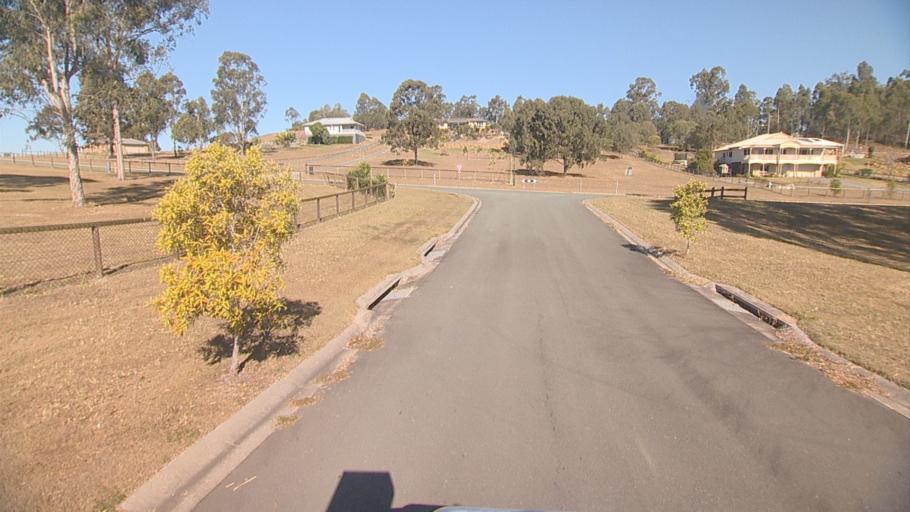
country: AU
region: Queensland
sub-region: Logan
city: Cedar Vale
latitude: -27.8683
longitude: 153.0338
